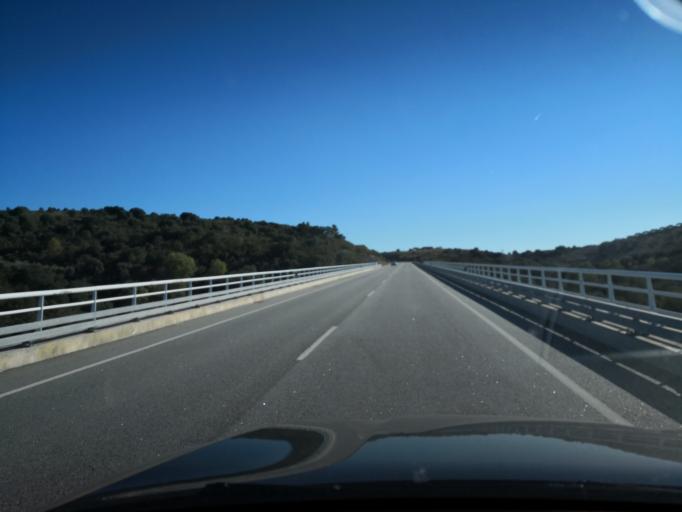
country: PT
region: Braganca
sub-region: Mirandela
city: Mirandela
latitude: 41.5059
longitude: -7.2296
